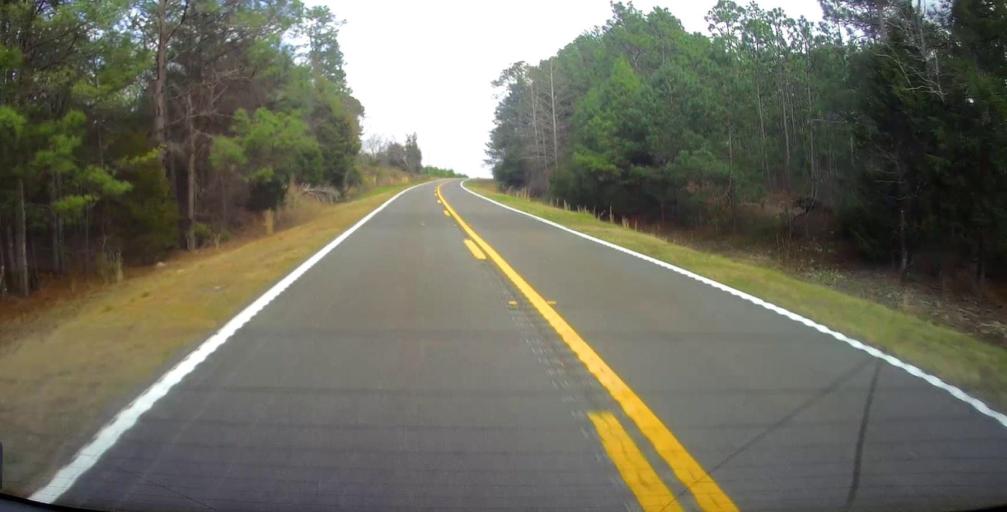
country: US
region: Georgia
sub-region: Marion County
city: Buena Vista
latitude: 32.4466
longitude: -84.4657
